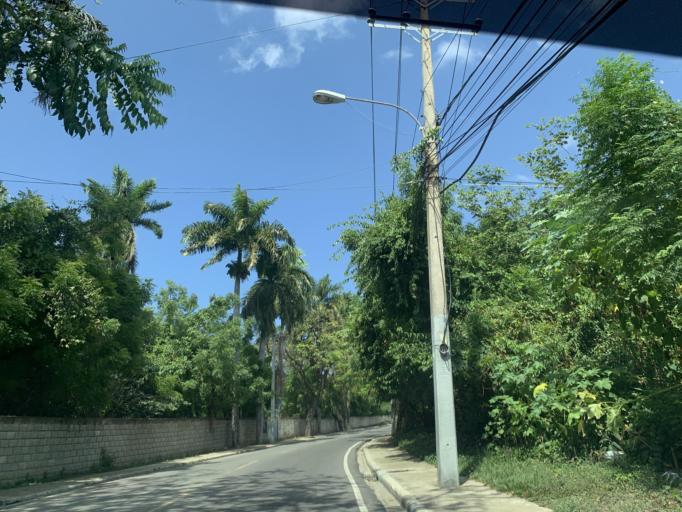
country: DO
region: Puerto Plata
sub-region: Puerto Plata
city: Puerto Plata
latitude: 19.8038
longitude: -70.7179
